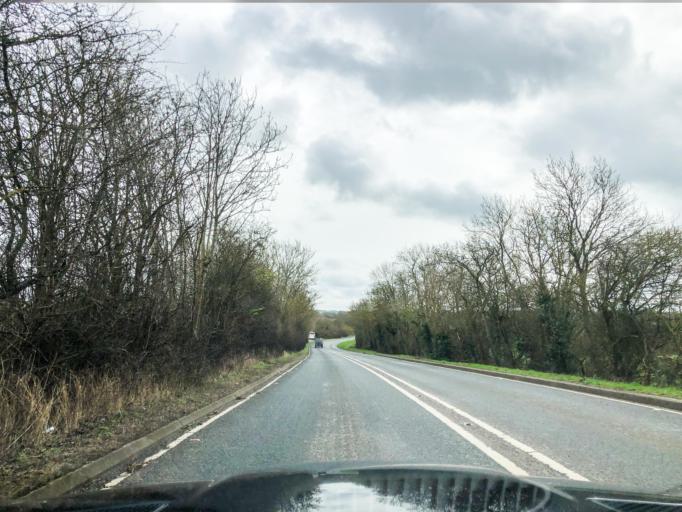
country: GB
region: England
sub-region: Warwickshire
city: Harbury
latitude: 52.1799
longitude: -1.4624
